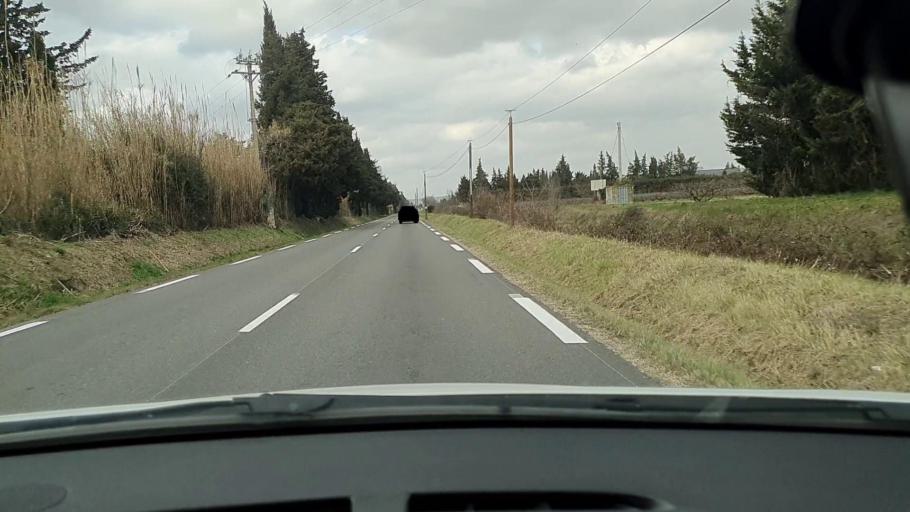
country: FR
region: Languedoc-Roussillon
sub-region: Departement du Gard
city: Montfrin
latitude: 43.8727
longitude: 4.5822
